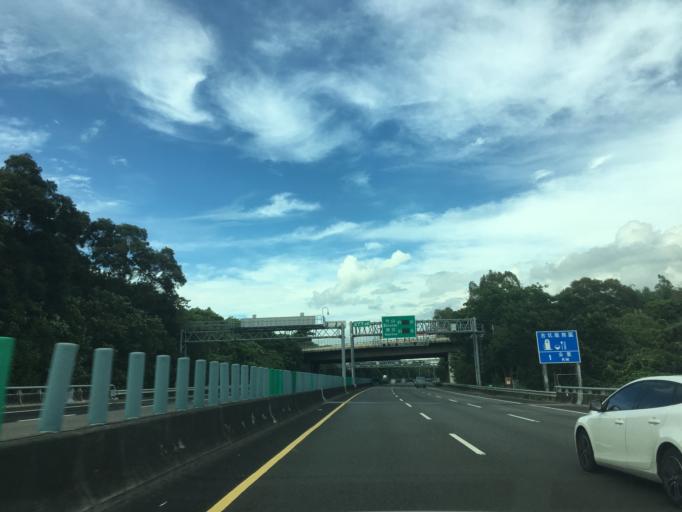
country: TW
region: Taiwan
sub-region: Yunlin
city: Douliu
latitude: 23.6054
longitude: 120.5304
